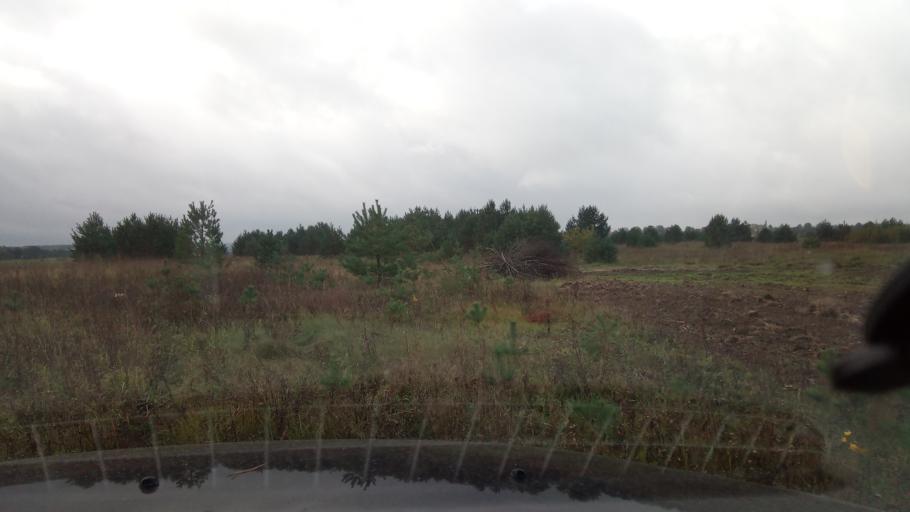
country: LT
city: Skaidiskes
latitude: 54.6223
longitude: 25.5216
